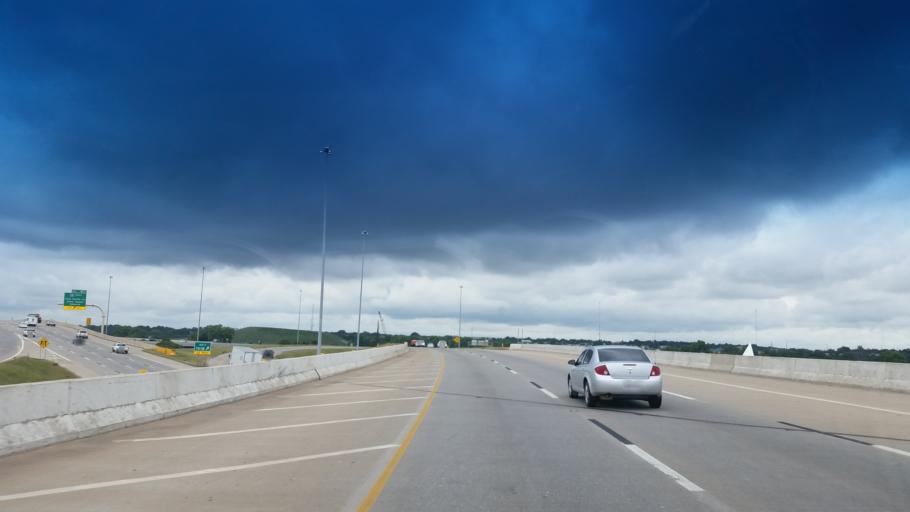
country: US
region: Oklahoma
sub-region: Oklahoma County
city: Oklahoma City
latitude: 35.4626
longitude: -97.4968
